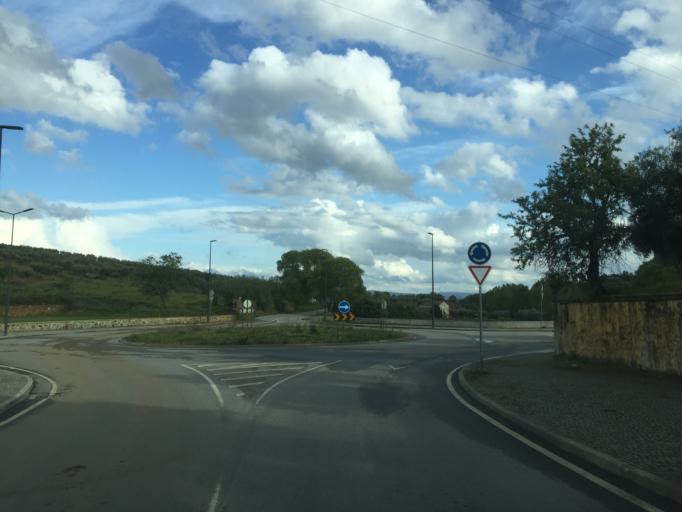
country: PT
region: Braganca
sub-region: Alfandega da Fe
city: Alfandega da Fe
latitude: 41.3404
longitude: -6.9603
